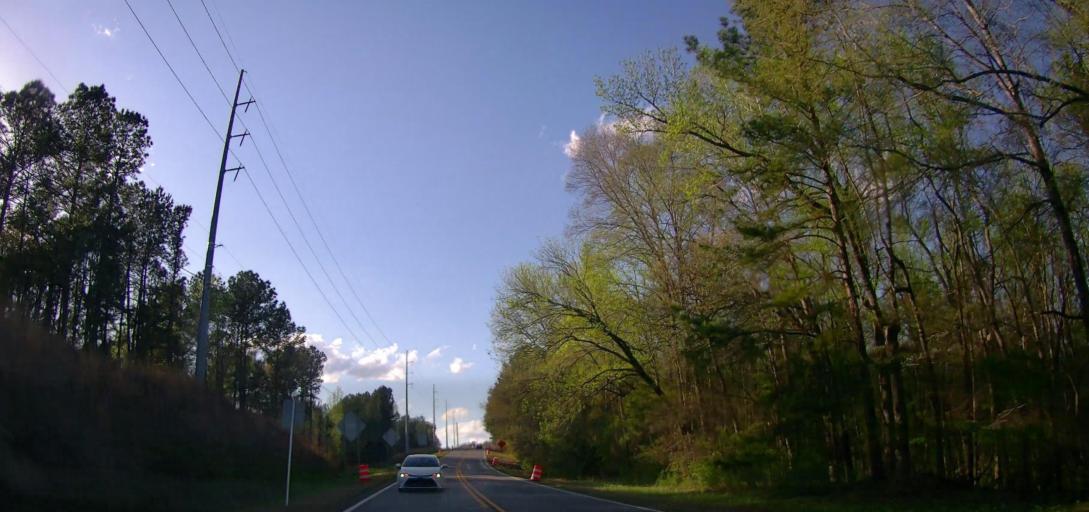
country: US
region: Georgia
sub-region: Baldwin County
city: Milledgeville
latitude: 33.1020
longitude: -83.2738
